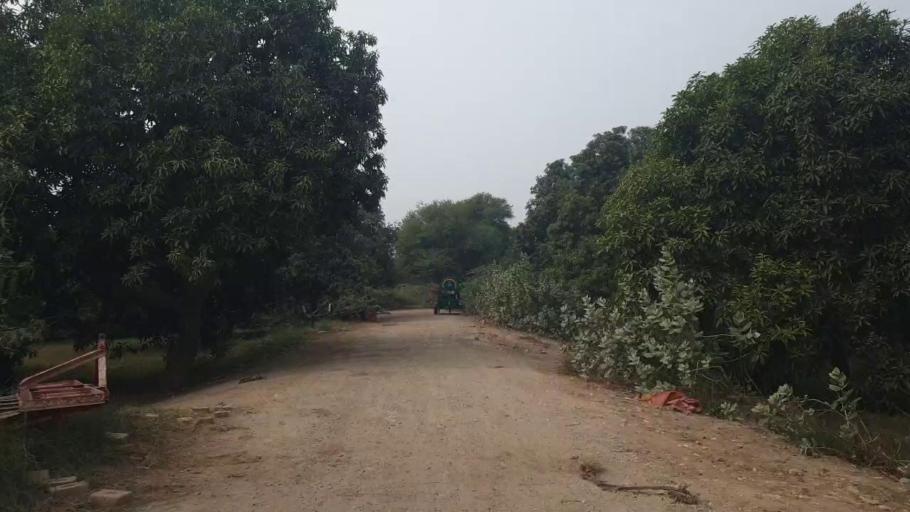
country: PK
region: Sindh
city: Tando Adam
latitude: 25.7867
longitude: 68.6639
